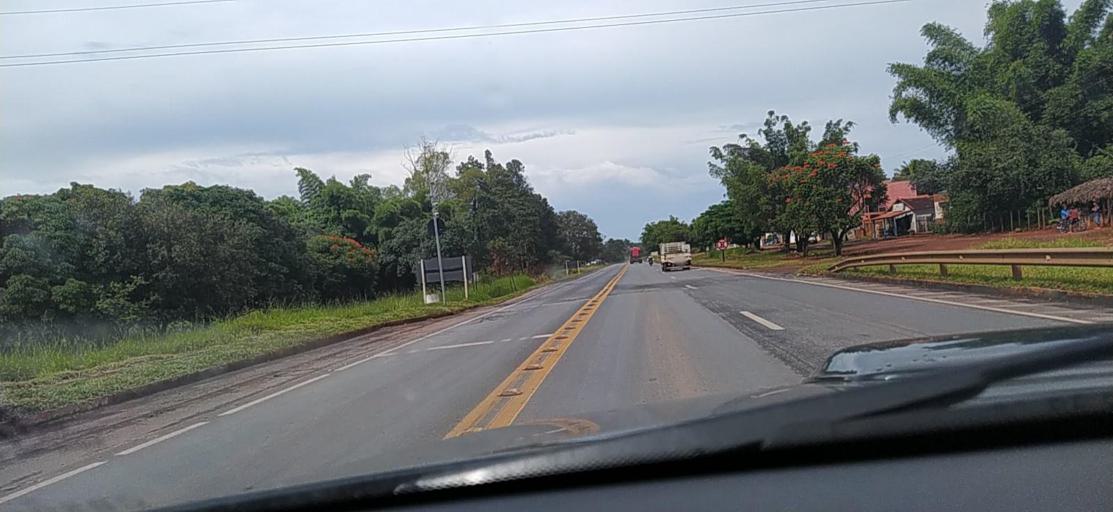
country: BR
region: Minas Gerais
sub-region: Montes Claros
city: Montes Claros
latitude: -16.8787
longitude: -43.8625
